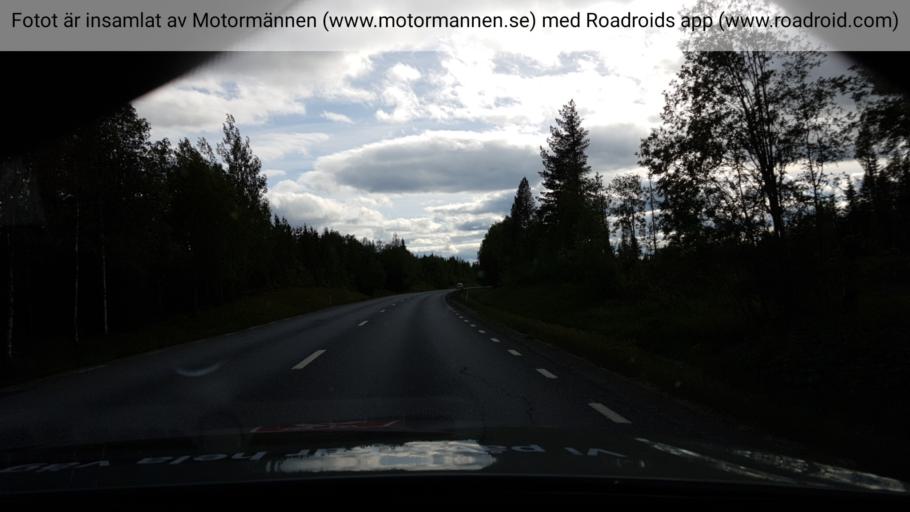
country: SE
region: Jaemtland
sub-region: OEstersunds Kommun
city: Lit
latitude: 63.4181
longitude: 15.1029
